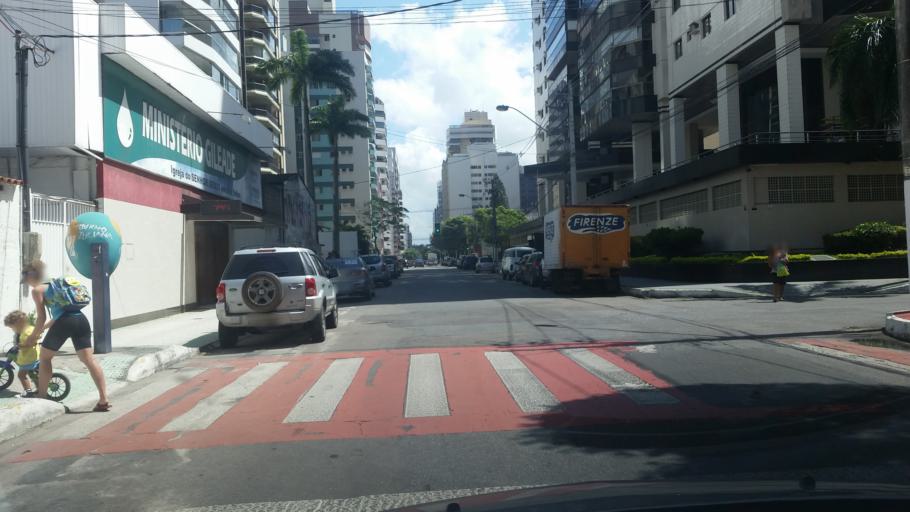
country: BR
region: Espirito Santo
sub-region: Vila Velha
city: Vila Velha
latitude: -20.3459
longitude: -40.2861
